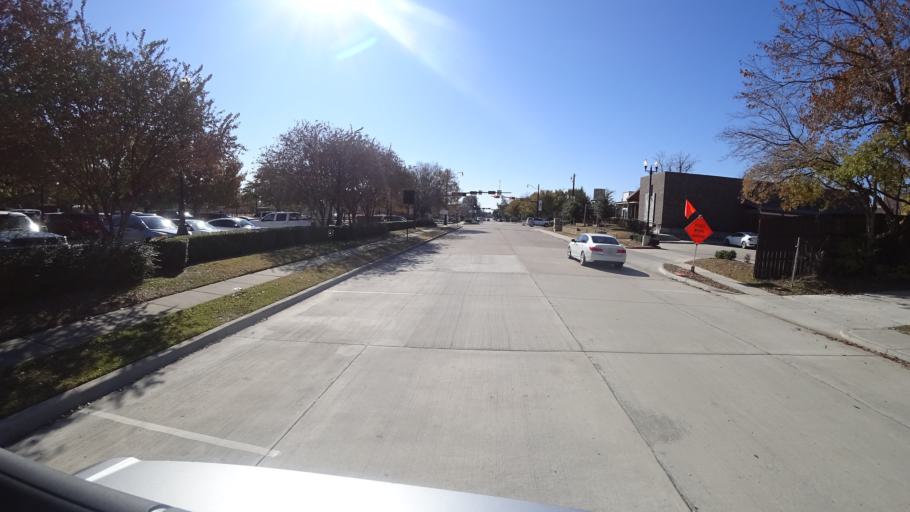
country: US
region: Texas
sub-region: Denton County
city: Lewisville
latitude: 33.0479
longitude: -96.9965
